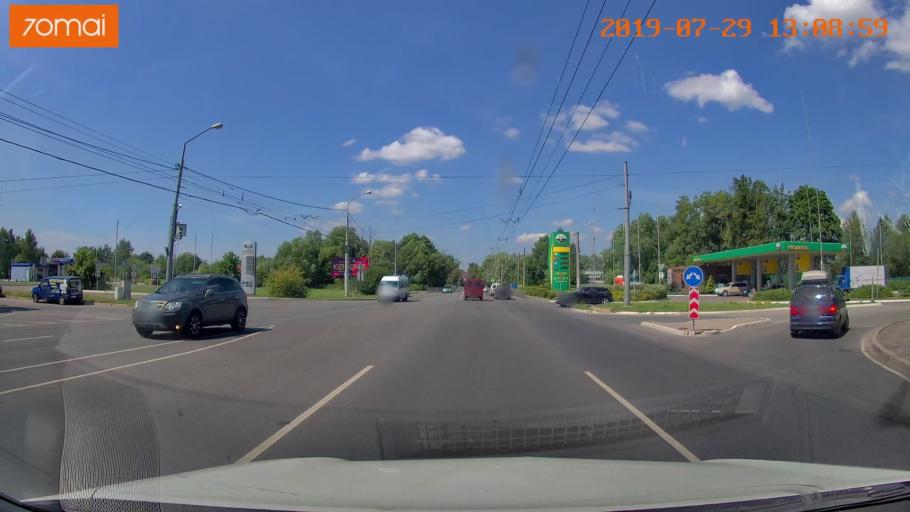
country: RU
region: Kaliningrad
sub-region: Gorod Kaliningrad
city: Kaliningrad
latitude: 54.7128
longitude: 20.4231
